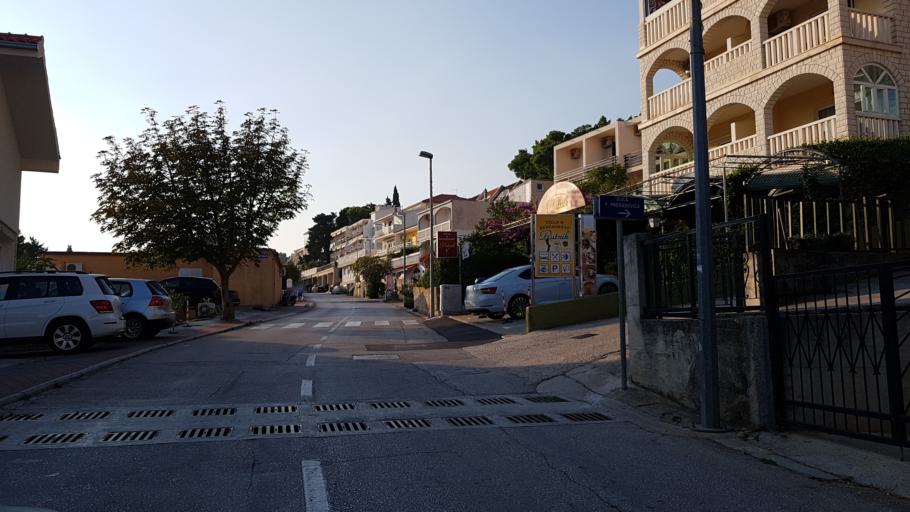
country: HR
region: Splitsko-Dalmatinska
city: Baska Voda
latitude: 43.3594
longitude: 16.9496
